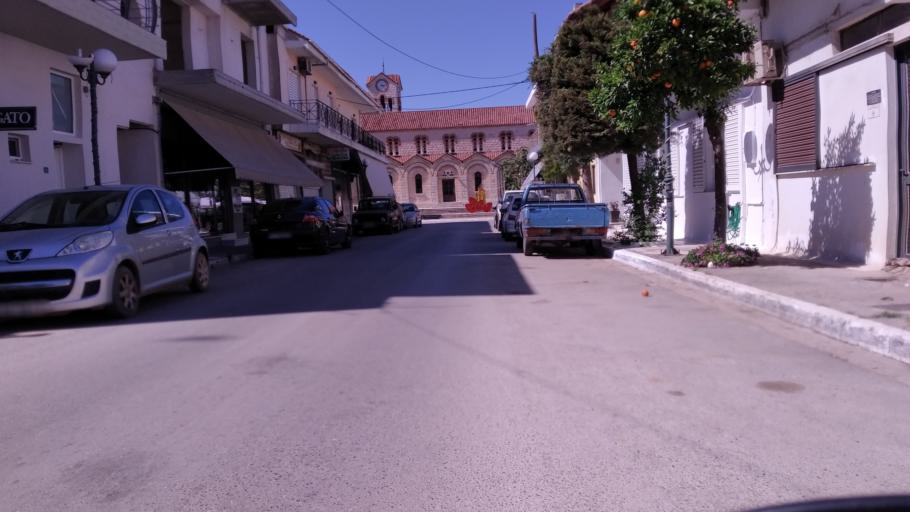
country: GR
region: Central Greece
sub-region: Nomos Fthiotidos
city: Malesina
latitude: 38.6223
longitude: 23.2315
